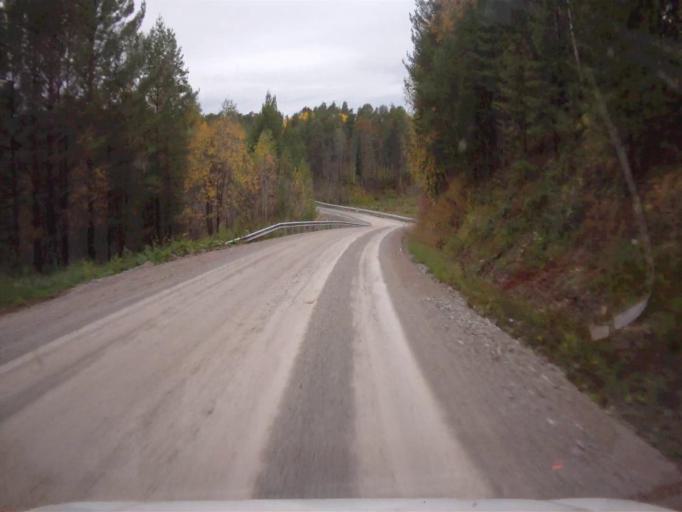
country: RU
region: Chelyabinsk
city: Nyazepetrovsk
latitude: 56.0594
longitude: 59.4527
